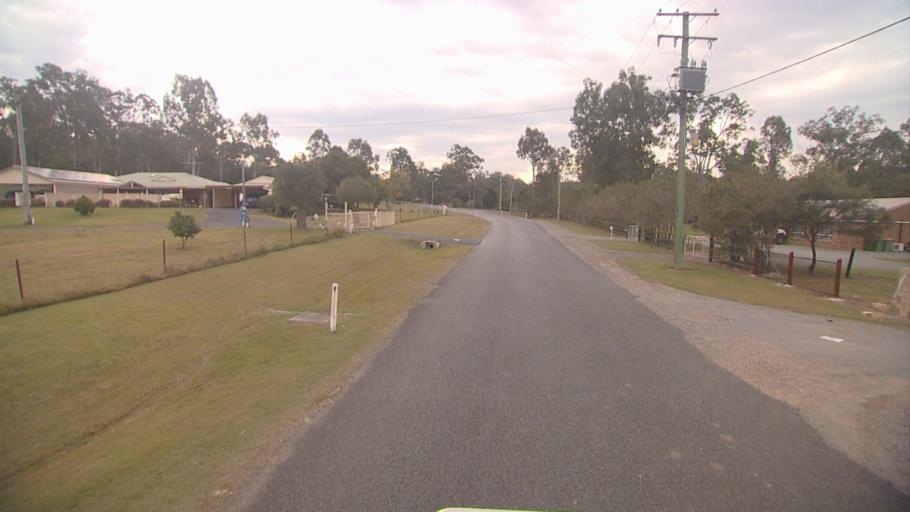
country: AU
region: Queensland
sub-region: Logan
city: Chambers Flat
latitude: -27.7902
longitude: 153.1156
